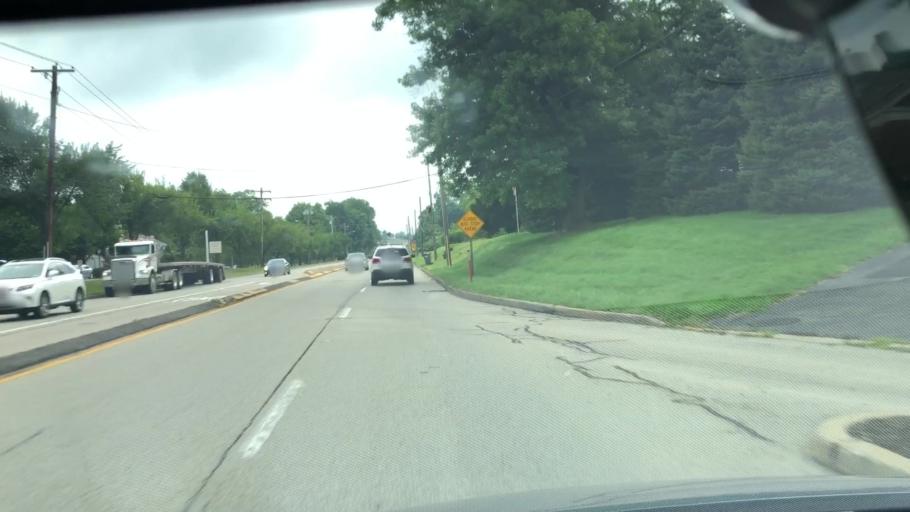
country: US
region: Pennsylvania
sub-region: Allegheny County
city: Upper Saint Clair
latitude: 40.3390
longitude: -80.0657
